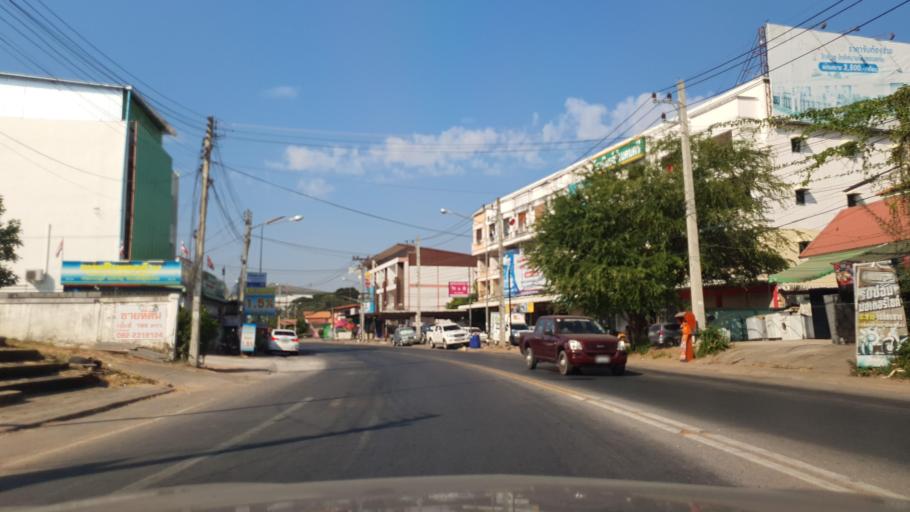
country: TH
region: Khon Kaen
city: Khon Kaen
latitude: 16.4348
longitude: 102.8173
